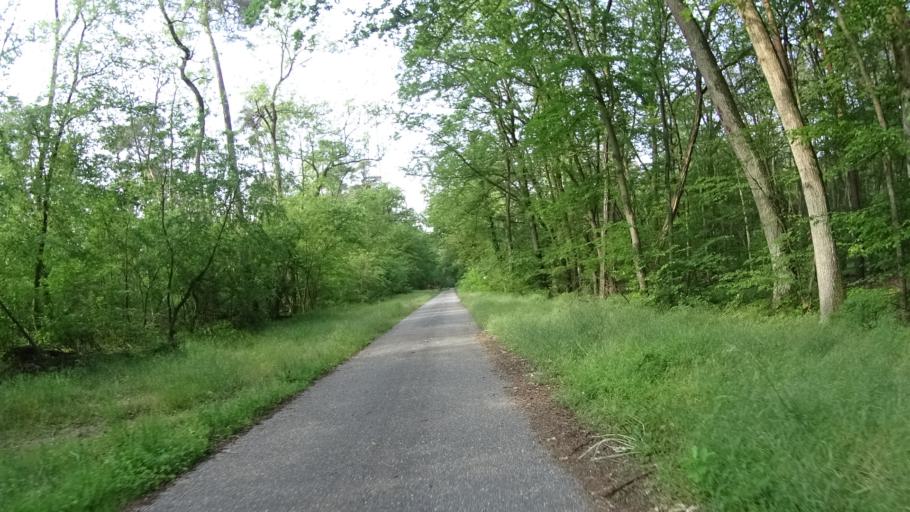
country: DE
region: Baden-Wuerttemberg
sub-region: Karlsruhe Region
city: Sandhausen
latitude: 49.3424
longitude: 8.6300
